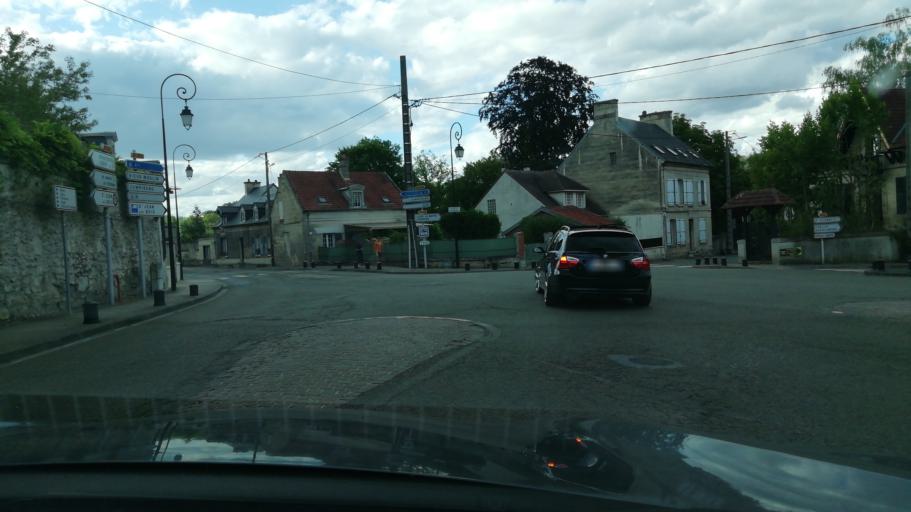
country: FR
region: Picardie
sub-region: Departement de l'Oise
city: Pierrefonds
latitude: 49.3507
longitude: 2.9810
